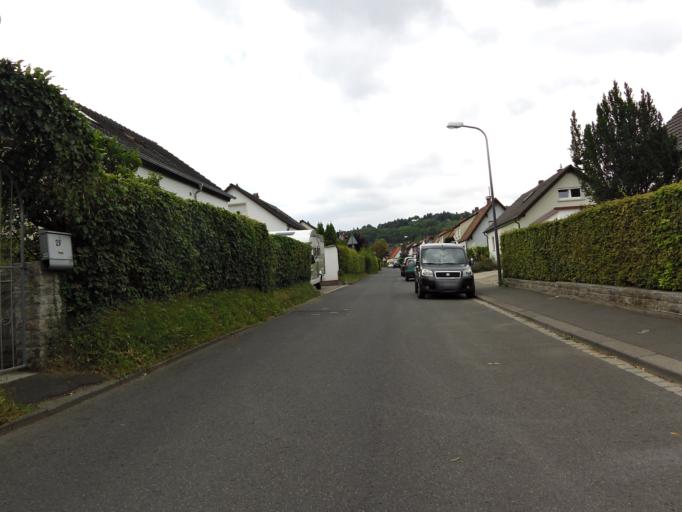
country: DE
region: Bavaria
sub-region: Regierungsbezirk Unterfranken
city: Wuerzburg
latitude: 49.7612
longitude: 9.9378
